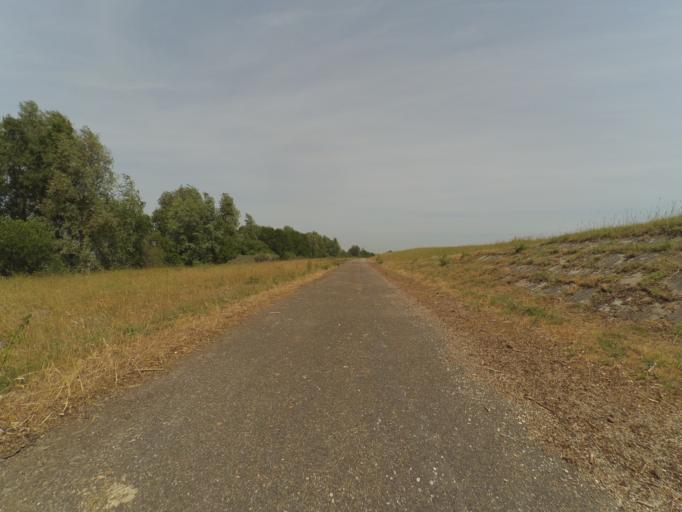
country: NL
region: North Brabant
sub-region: Gemeente Steenbergen
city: Nieuw-Vossemeer
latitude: 51.6071
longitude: 4.1929
